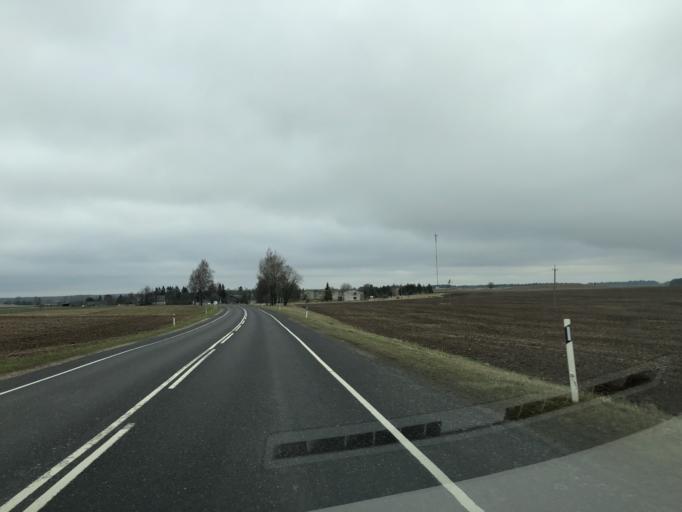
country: EE
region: Laeaene-Virumaa
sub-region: Vaeike-Maarja vald
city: Vaike-Maarja
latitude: 59.2199
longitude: 26.2682
